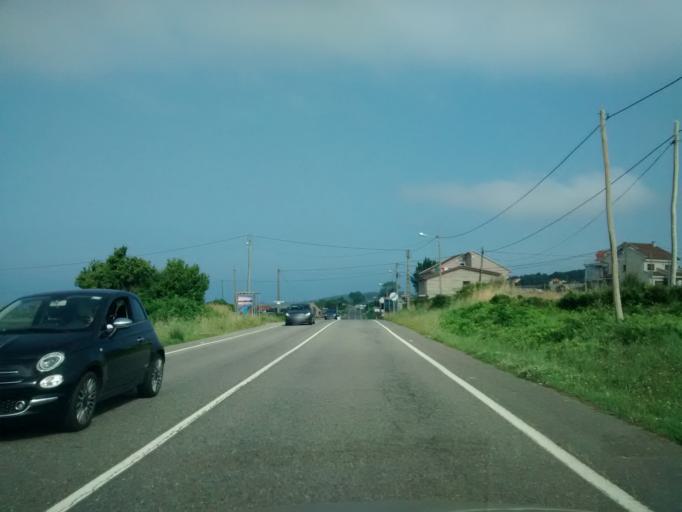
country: ES
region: Galicia
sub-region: Provincia de Pontevedra
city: Sanxenxo
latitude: 42.4090
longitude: -8.8561
